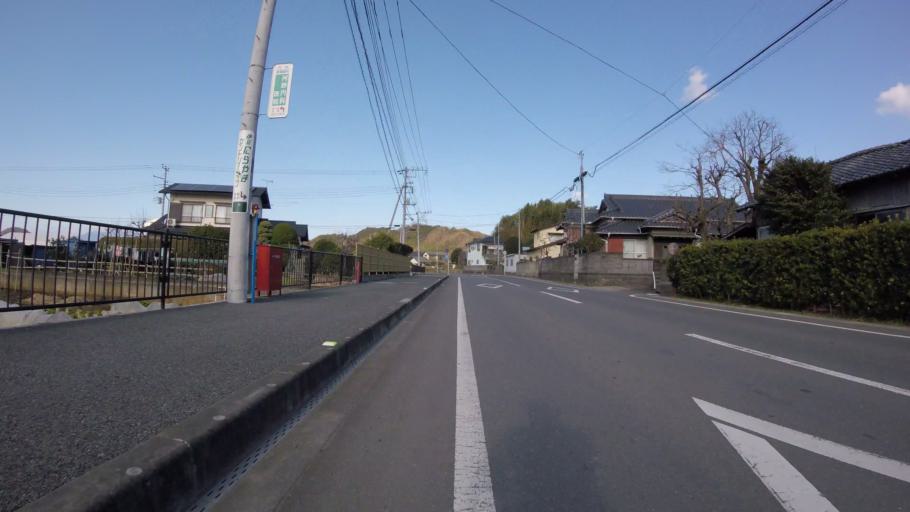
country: JP
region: Shizuoka
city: Mishima
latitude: 35.0394
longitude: 138.9584
